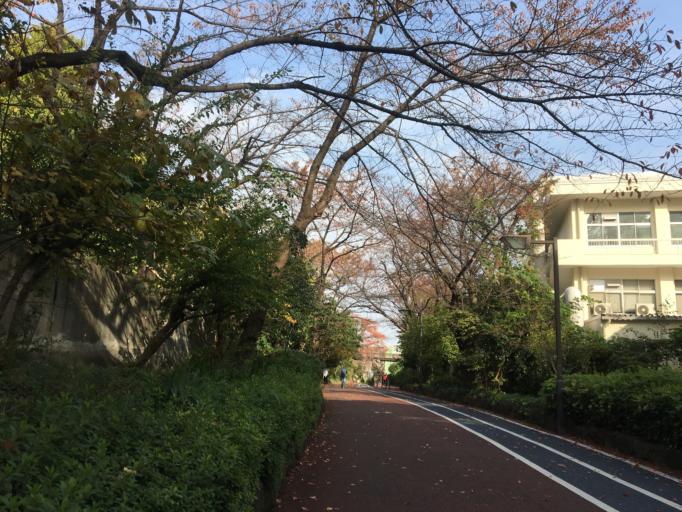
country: JP
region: Tokyo
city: Tokyo
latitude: 35.6068
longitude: 139.6802
